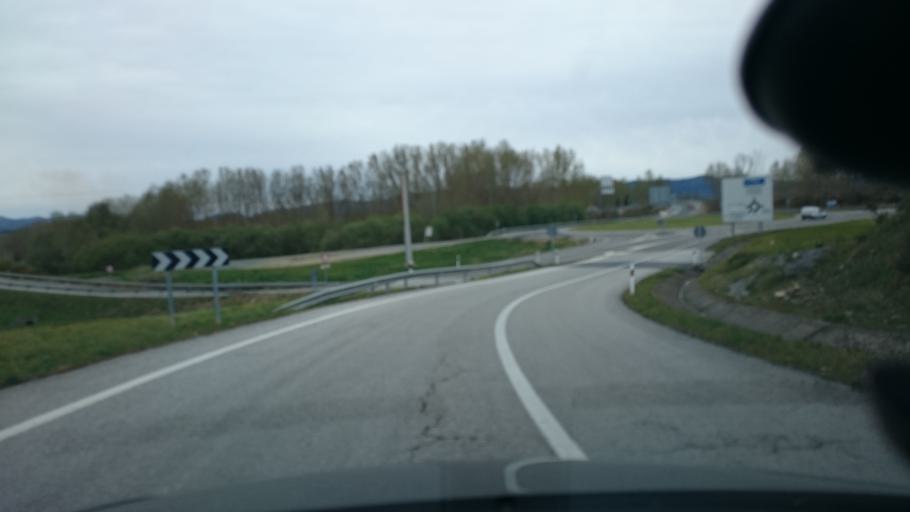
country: ES
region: Castille and Leon
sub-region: Provincia de Leon
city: Carracedelo
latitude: 42.5645
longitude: -6.7291
